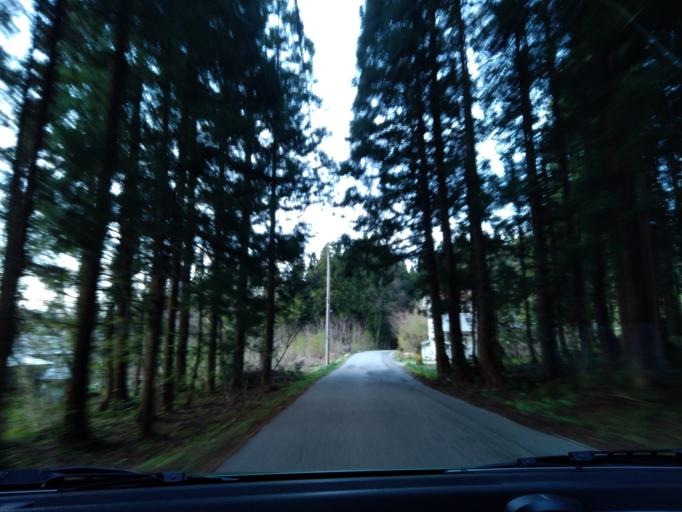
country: JP
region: Akita
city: Kakunodatemachi
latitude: 39.5902
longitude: 140.5775
